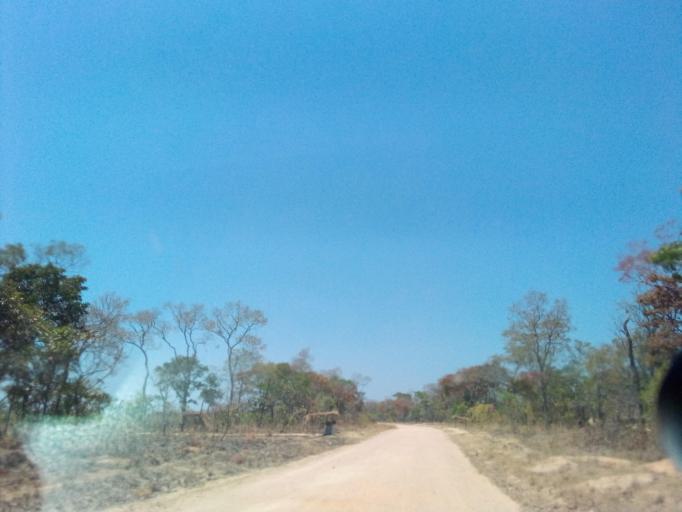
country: ZM
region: Northern
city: Mpika
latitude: -12.2324
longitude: 30.6576
